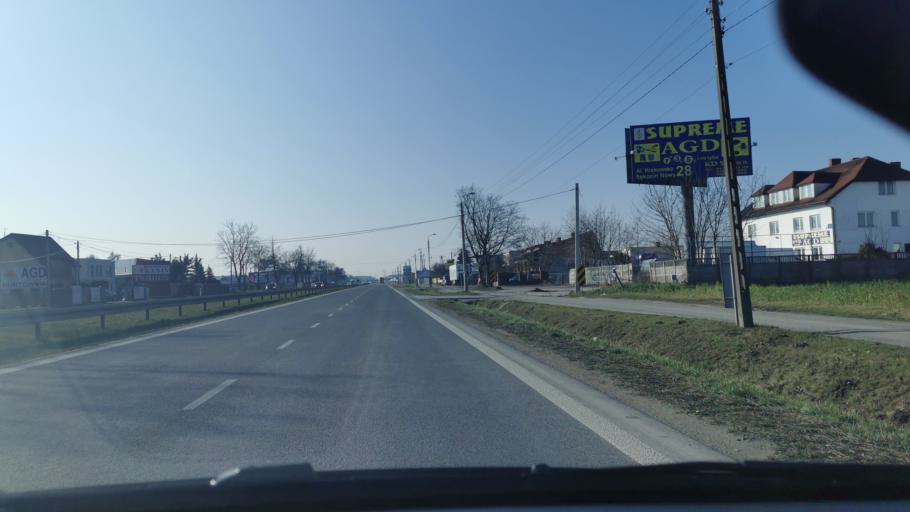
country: PL
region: Masovian Voivodeship
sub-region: Powiat pruszkowski
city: Nowe Grocholice
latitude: 52.1205
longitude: 20.8932
